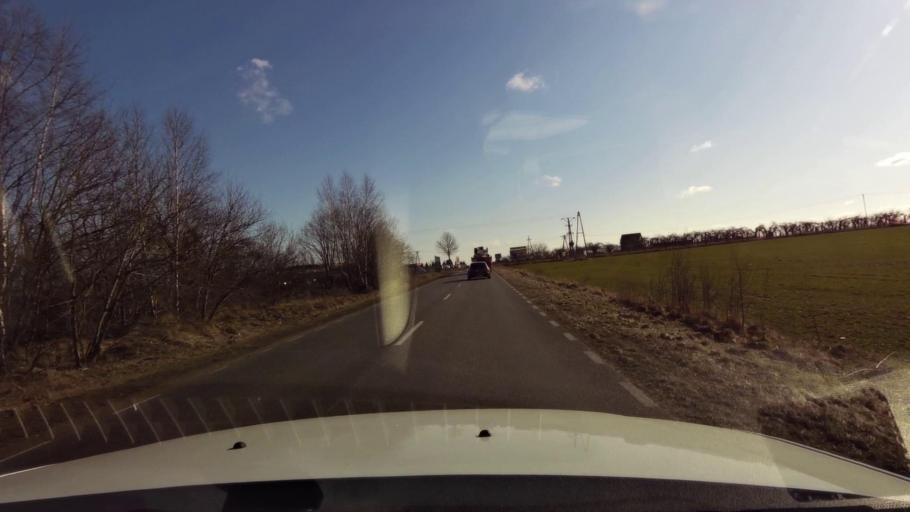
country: PL
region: West Pomeranian Voivodeship
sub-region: Powiat mysliborski
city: Barlinek
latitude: 52.9940
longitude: 15.1771
